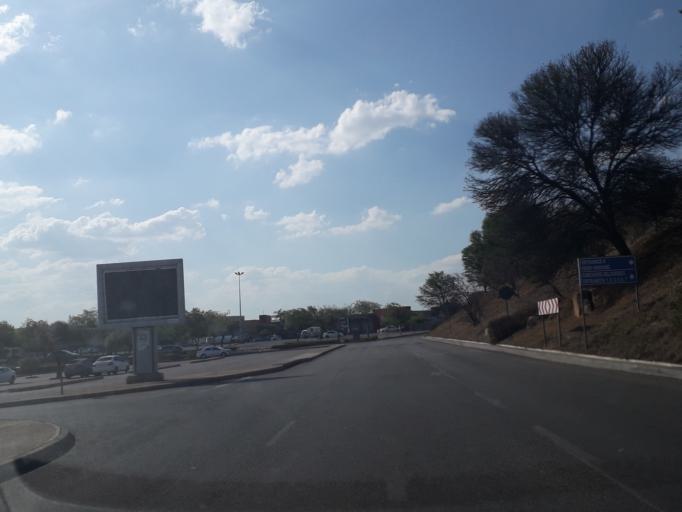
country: ZA
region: Gauteng
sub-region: West Rand District Municipality
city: Muldersdriseloop
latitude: -26.0612
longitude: 27.9488
